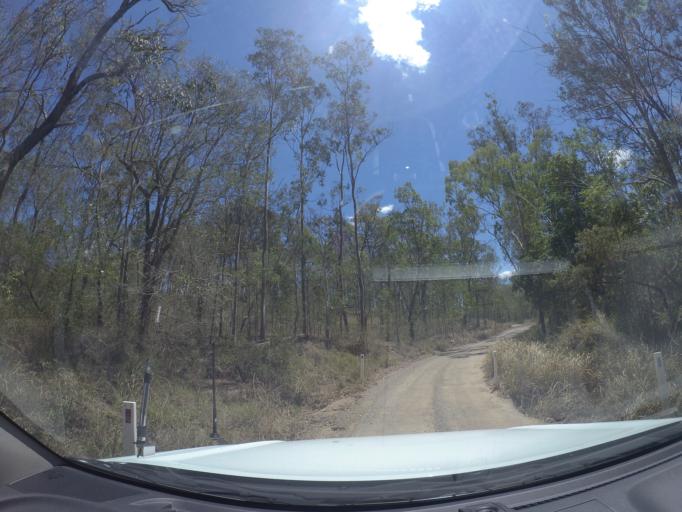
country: AU
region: Queensland
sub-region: Ipswich
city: Springfield Lakes
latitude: -27.8046
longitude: 152.8437
